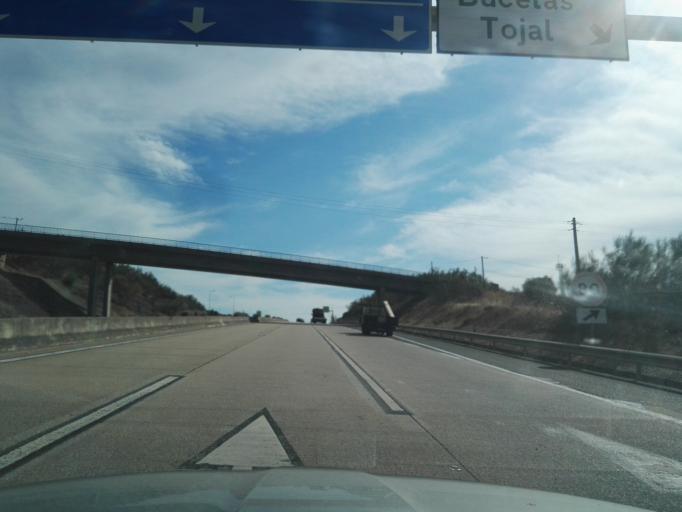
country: PT
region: Lisbon
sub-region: Loures
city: Santo Antao do Tojal
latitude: 38.8666
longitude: -9.1476
